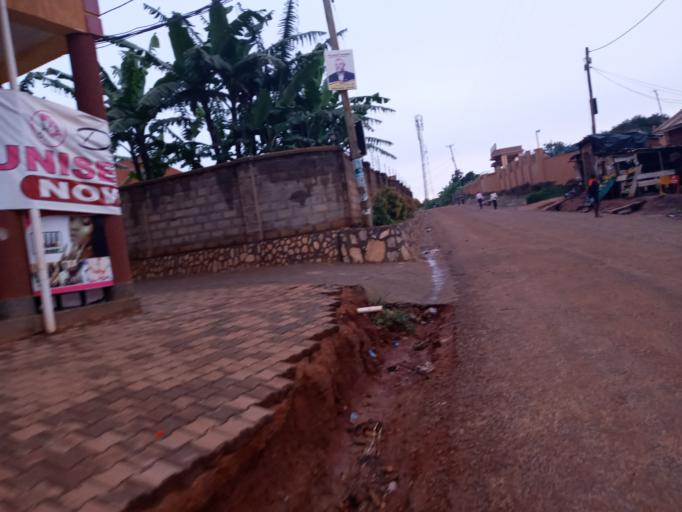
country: UG
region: Central Region
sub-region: Wakiso District
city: Bweyogerere
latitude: 0.3359
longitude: 32.6727
